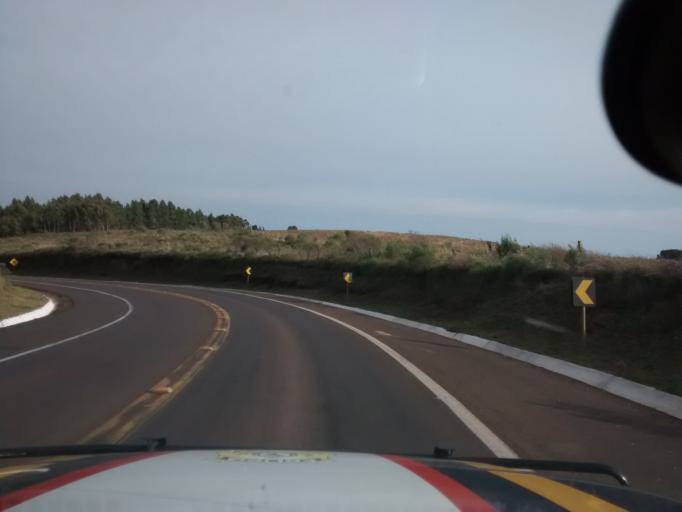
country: BR
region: Rio Grande do Sul
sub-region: Lagoa Vermelha
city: Lagoa Vermelha
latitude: -28.3190
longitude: -51.2468
